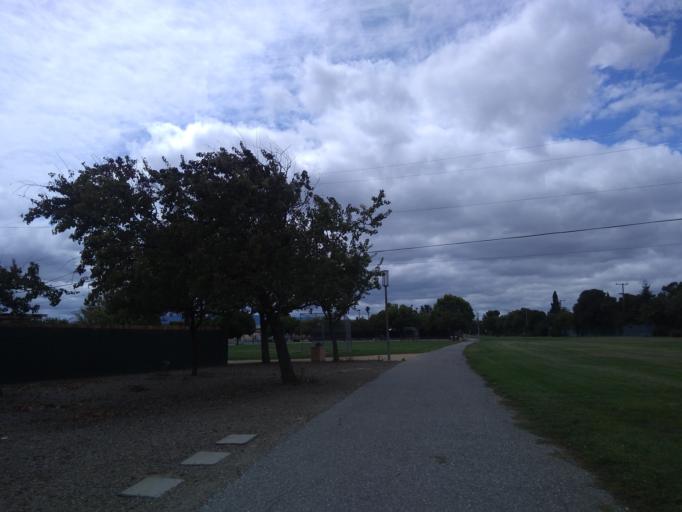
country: US
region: California
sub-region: Santa Clara County
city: Santa Clara
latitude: 37.3977
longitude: -121.9885
